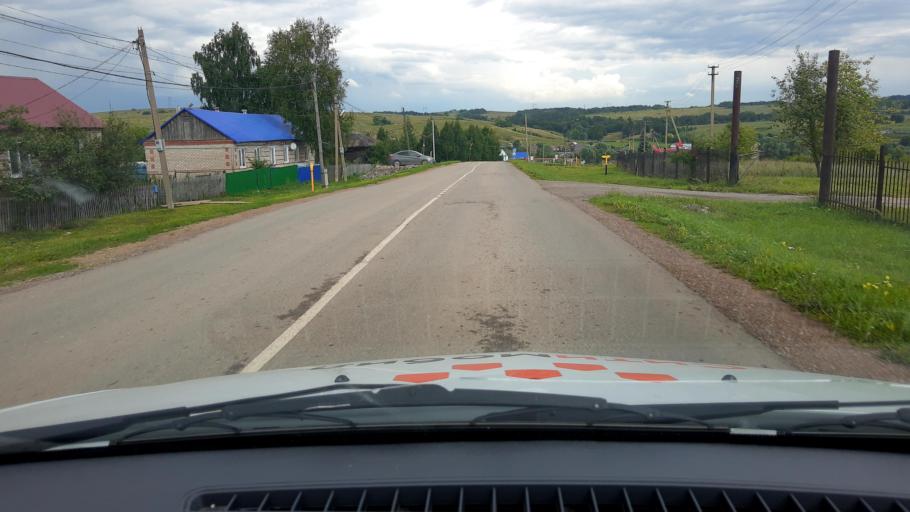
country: RU
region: Bashkortostan
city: Iglino
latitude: 54.9047
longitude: 56.1963
